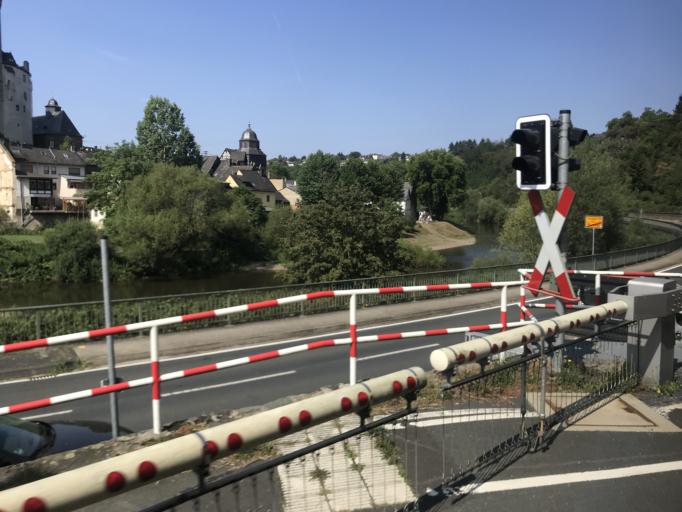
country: DE
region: Hesse
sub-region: Regierungsbezirk Giessen
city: Runkel
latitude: 50.4066
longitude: 8.1584
